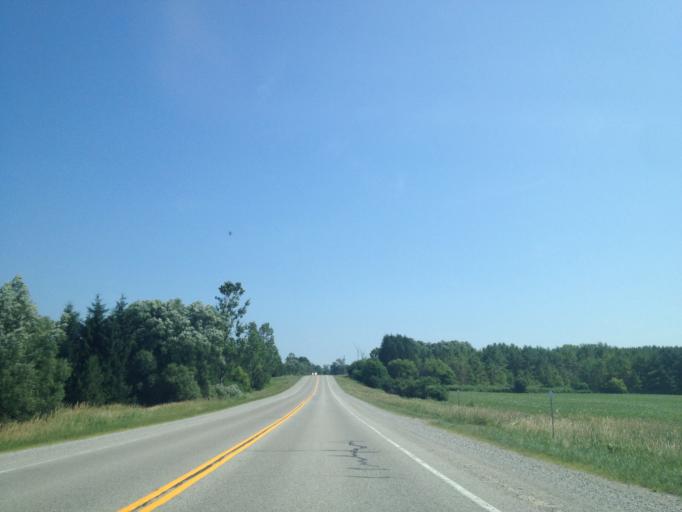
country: CA
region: Ontario
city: London
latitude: 43.2486
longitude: -81.2133
